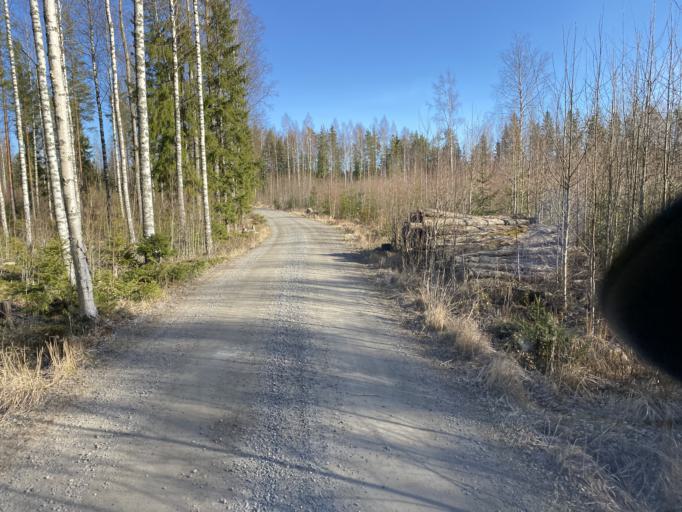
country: FI
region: Satakunta
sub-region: Rauma
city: Lappi
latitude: 61.1481
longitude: 21.8928
